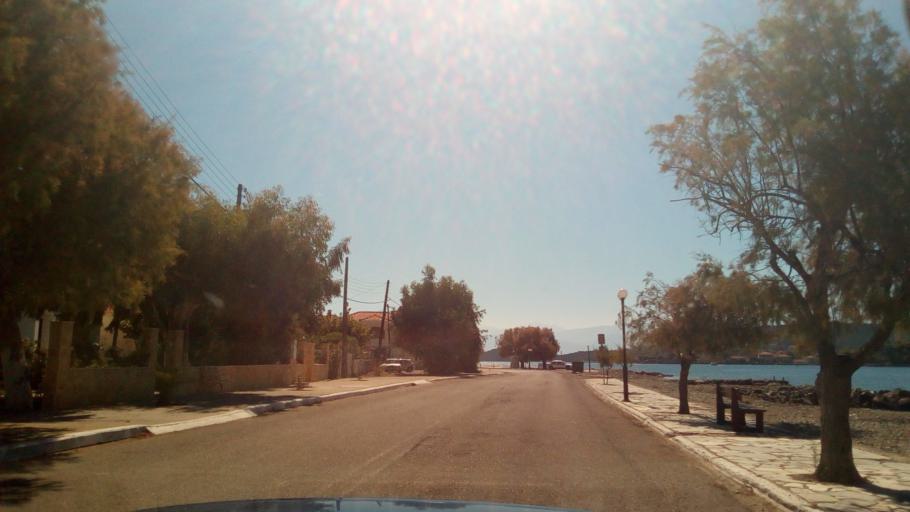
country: GR
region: West Greece
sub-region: Nomos Achaias
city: Selianitika
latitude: 38.3781
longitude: 22.0793
